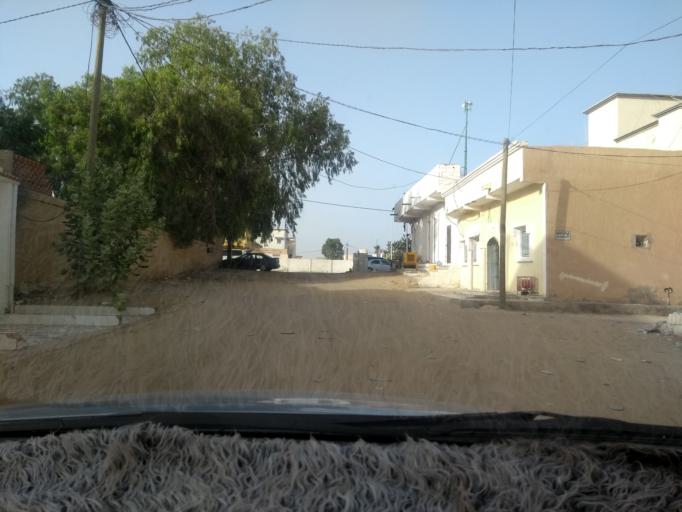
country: MR
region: Nouakchott
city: Nouakchott
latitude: 18.1081
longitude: -15.9742
